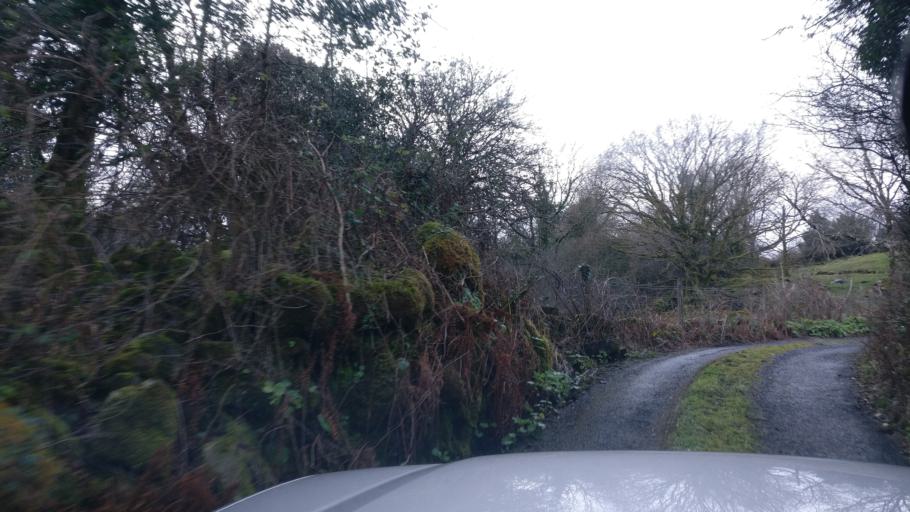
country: IE
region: Connaught
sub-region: County Galway
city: Oughterard
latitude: 53.5196
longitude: -9.4424
